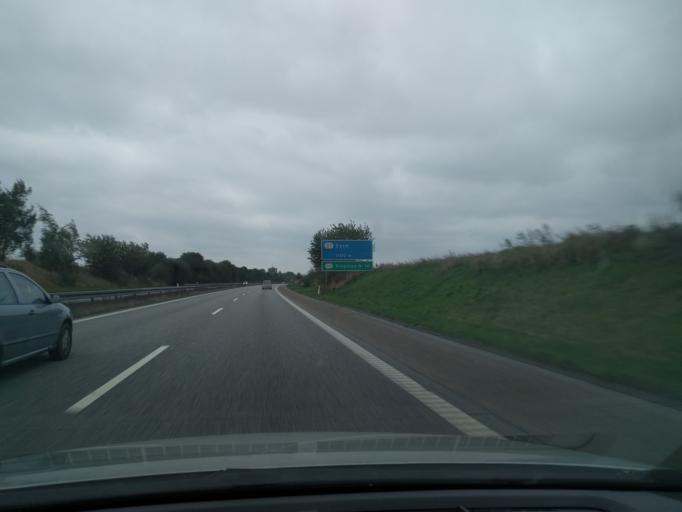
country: DK
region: Zealand
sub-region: Soro Kommune
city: Soro
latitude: 55.4524
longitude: 11.5378
